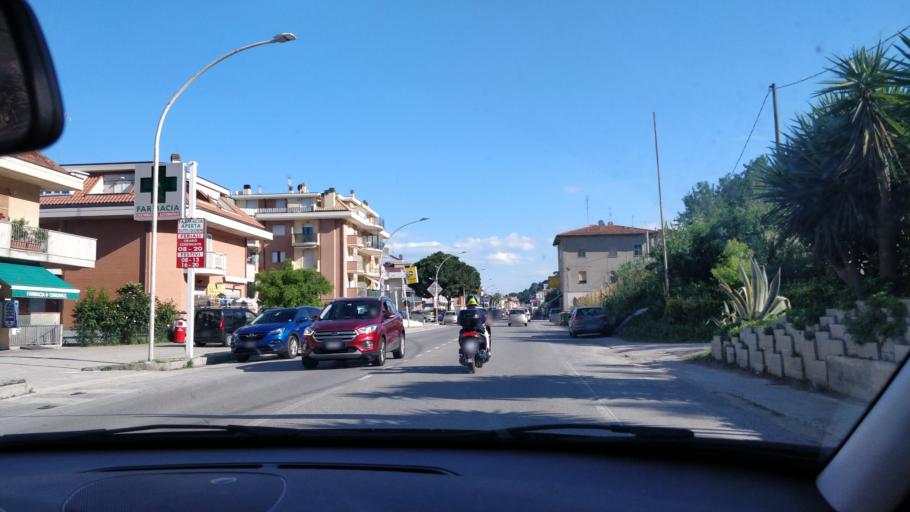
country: IT
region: The Marches
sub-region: Provincia di Ascoli Piceno
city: Cupra Marittima
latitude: 43.0325
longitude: 13.8564
